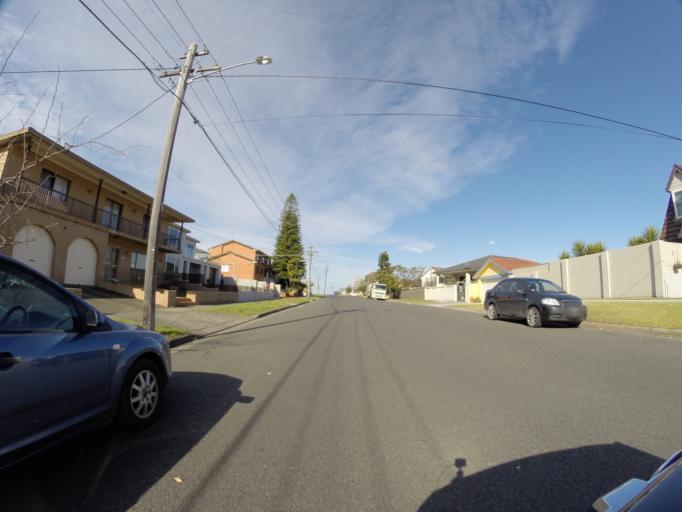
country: AU
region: New South Wales
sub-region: Randwick
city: South Coogee
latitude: -33.9394
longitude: 151.2501
